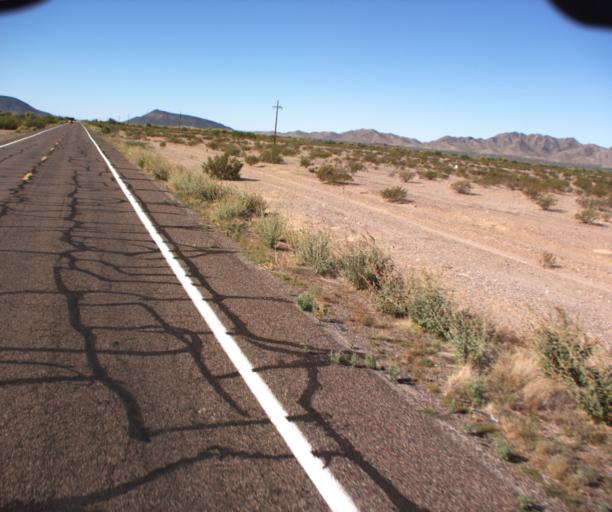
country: US
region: Arizona
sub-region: Maricopa County
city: Gila Bend
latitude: 32.8155
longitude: -112.7909
